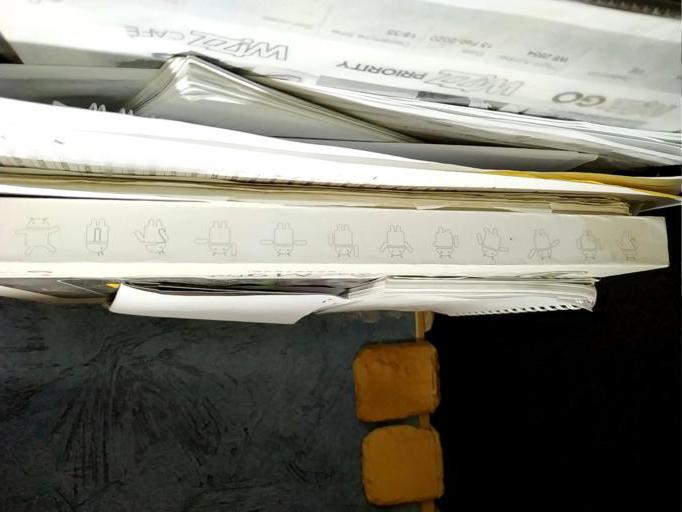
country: RU
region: Arkhangelskaya
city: Onega
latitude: 63.1829
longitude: 38.3324
